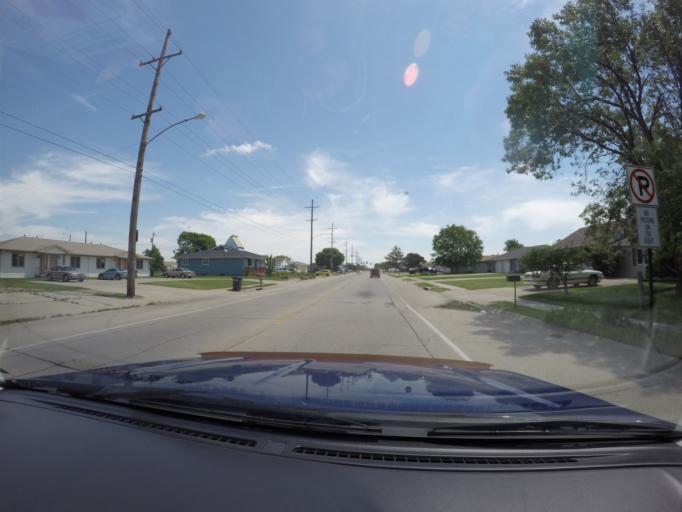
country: US
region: Nebraska
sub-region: Hall County
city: Grand Island
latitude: 40.9021
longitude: -98.3423
